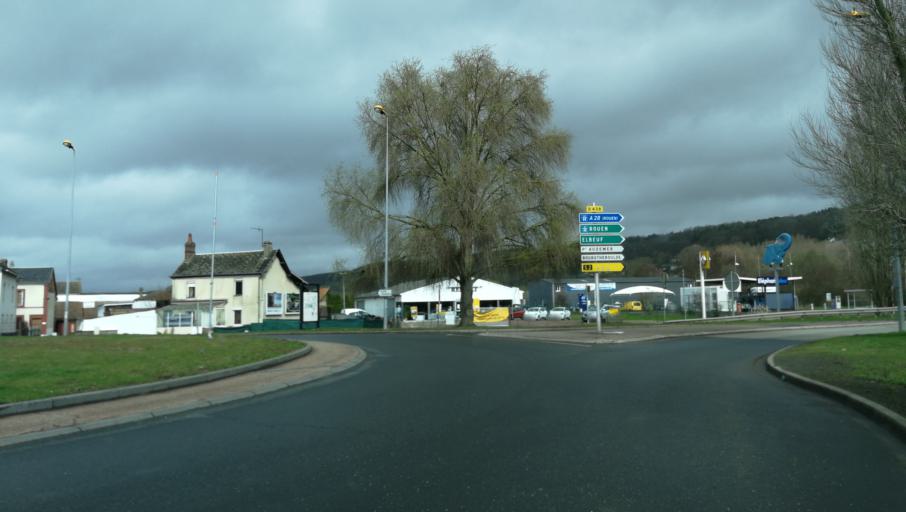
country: FR
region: Haute-Normandie
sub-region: Departement de l'Eure
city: Brionne
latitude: 49.1999
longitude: 0.7160
